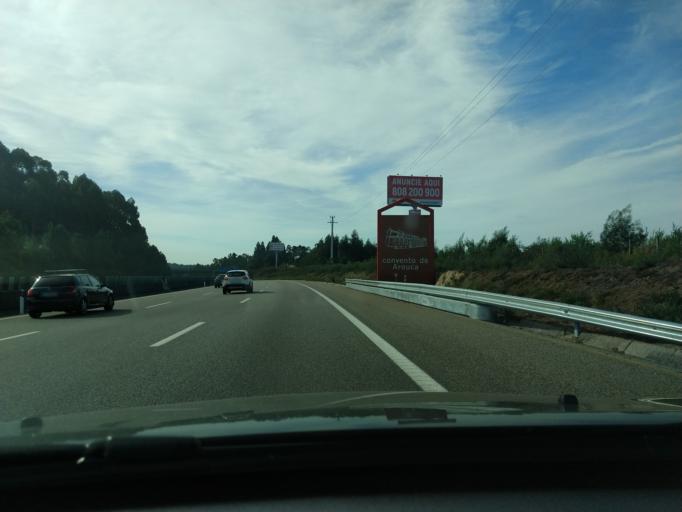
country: PT
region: Aveiro
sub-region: Santa Maria da Feira
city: Rio Meao
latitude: 40.9458
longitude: -8.5742
